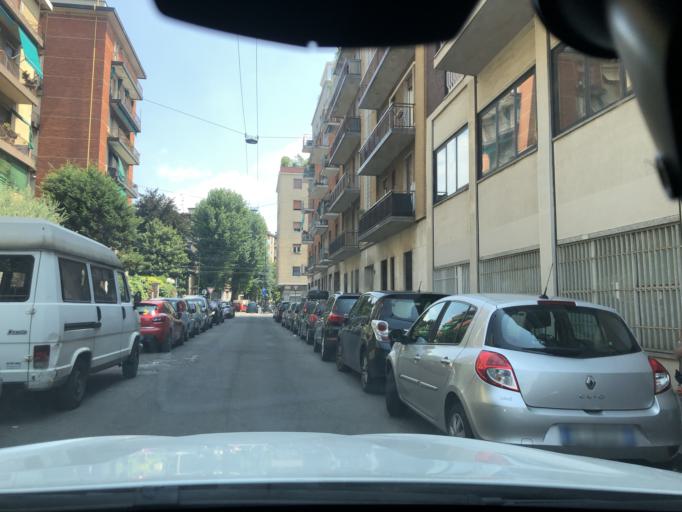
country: IT
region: Lombardy
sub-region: Citta metropolitana di Milano
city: Novate Milanese
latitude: 45.5004
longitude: 9.1664
